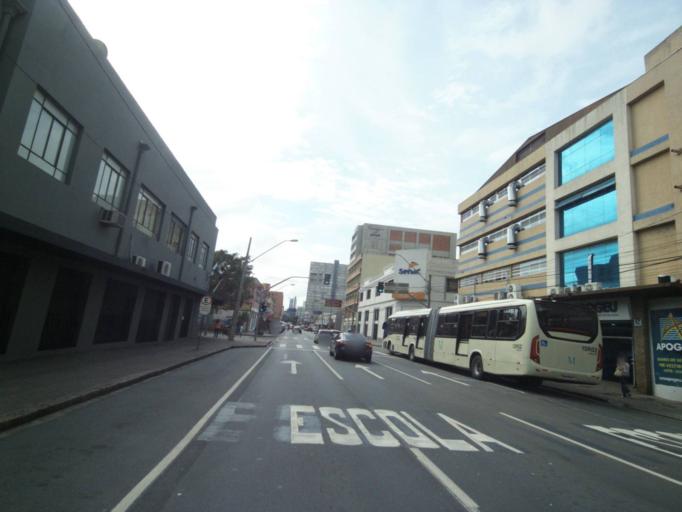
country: BR
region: Parana
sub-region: Curitiba
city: Curitiba
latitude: -25.4339
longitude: -49.2666
